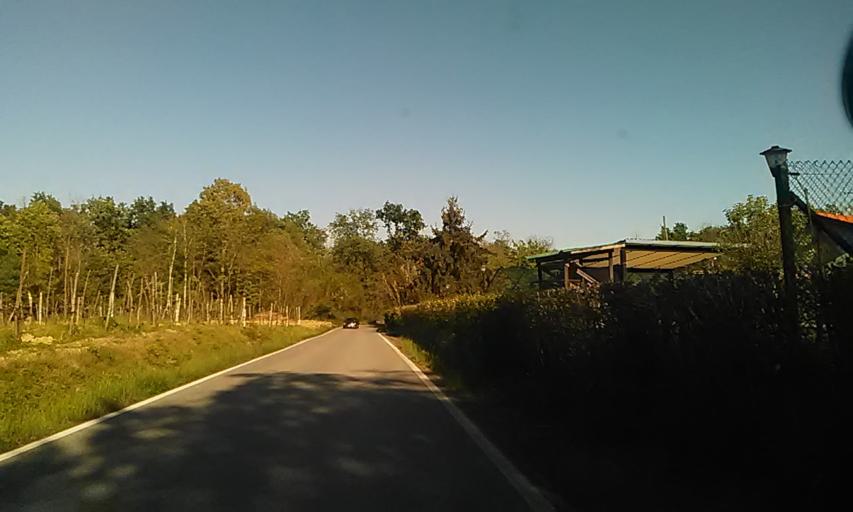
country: IT
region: Piedmont
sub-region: Provincia di Novara
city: Cavaglio D'Agogna
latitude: 45.6153
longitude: 8.4634
